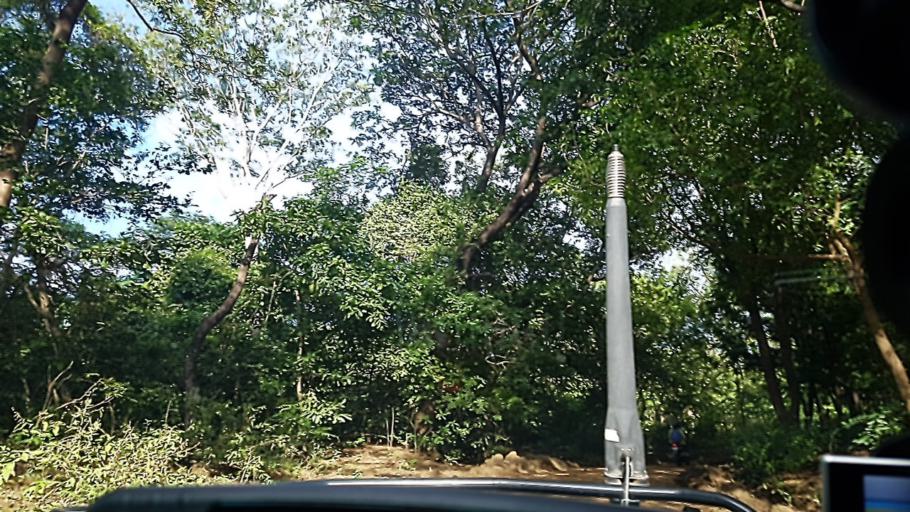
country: NI
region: Rivas
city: Tola
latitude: 11.5226
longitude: -86.1410
